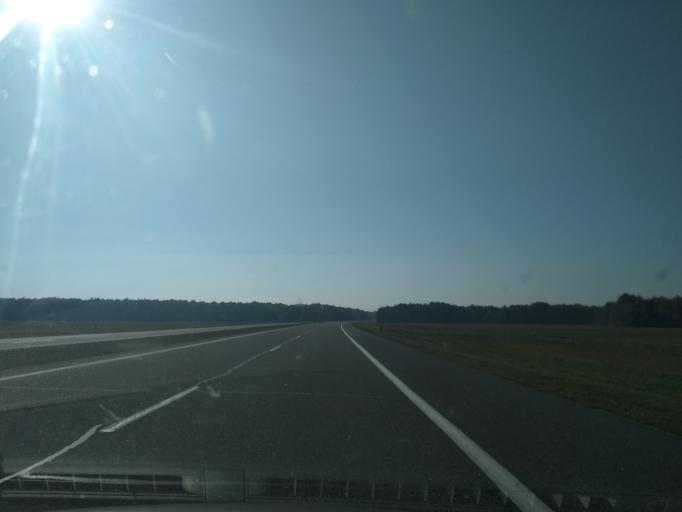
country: BY
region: Brest
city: Horad Kobryn
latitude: 52.2879
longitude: 24.5682
